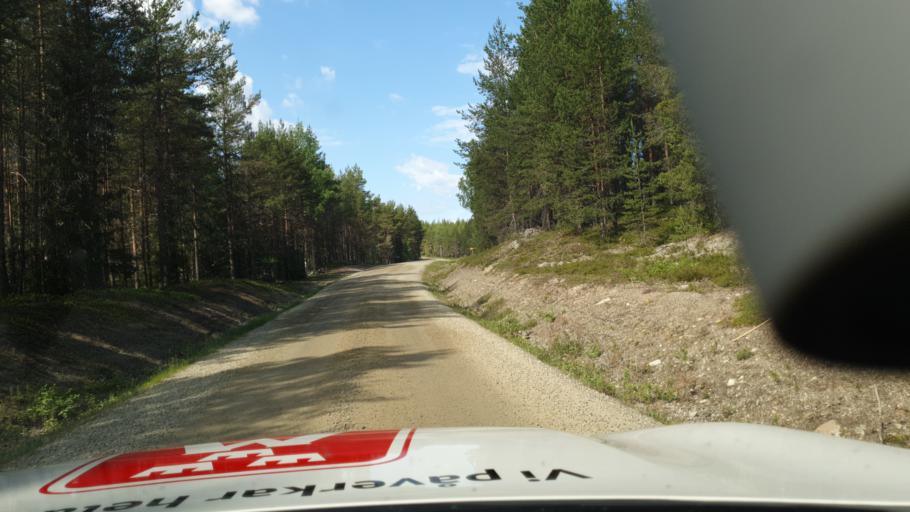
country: SE
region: Vaesterbotten
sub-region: Norsjo Kommun
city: Norsjoe
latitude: 64.6969
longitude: 19.4524
